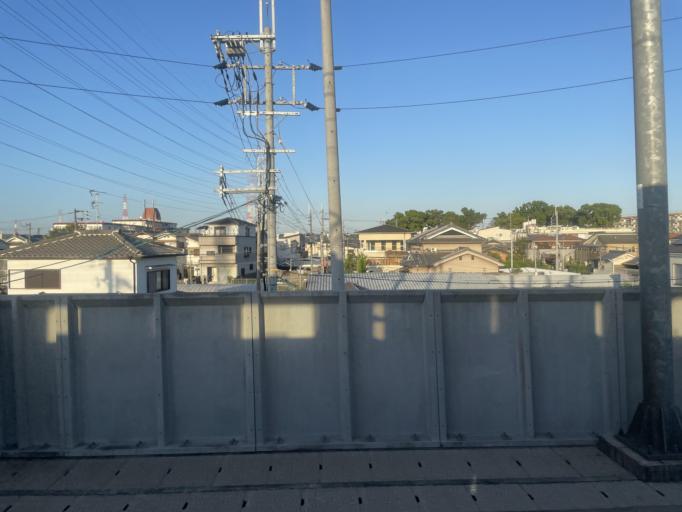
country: JP
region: Osaka
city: Matsubara
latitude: 34.5949
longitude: 135.5328
